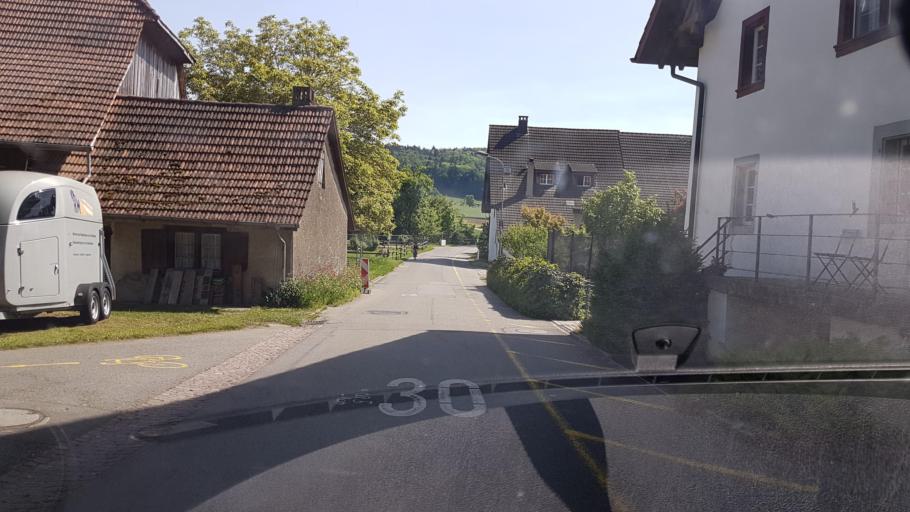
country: CH
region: Aargau
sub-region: Bezirk Baden
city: Wurenlos
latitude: 47.4489
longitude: 8.3766
